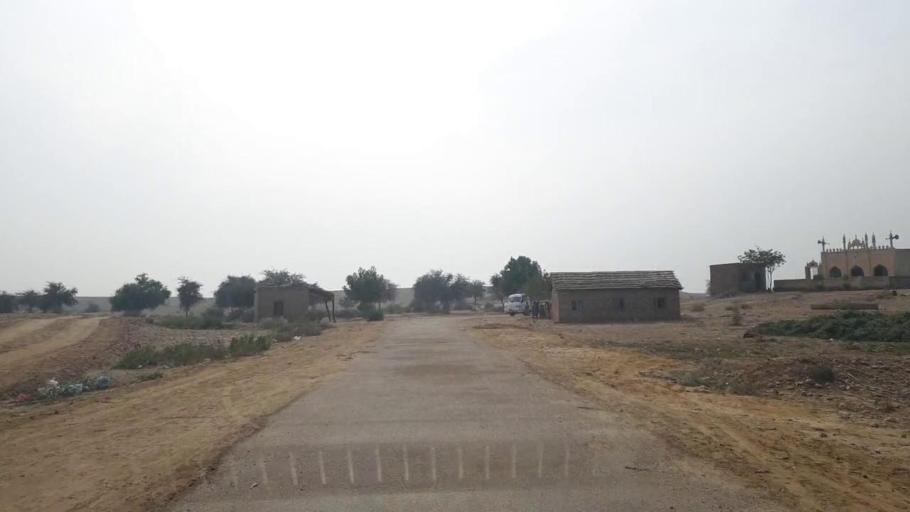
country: PK
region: Sindh
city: Sann
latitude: 26.0024
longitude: 68.1401
